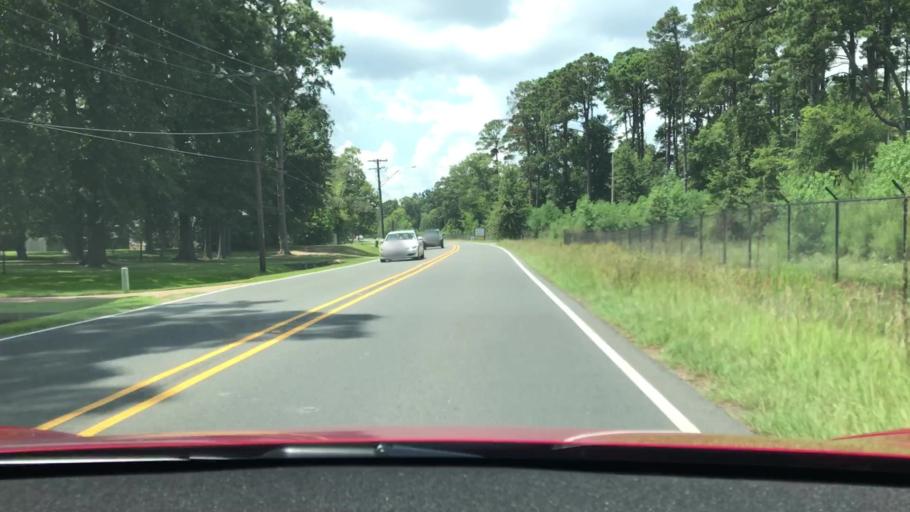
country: US
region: Louisiana
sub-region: Bossier Parish
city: Bossier City
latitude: 32.3860
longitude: -93.7172
